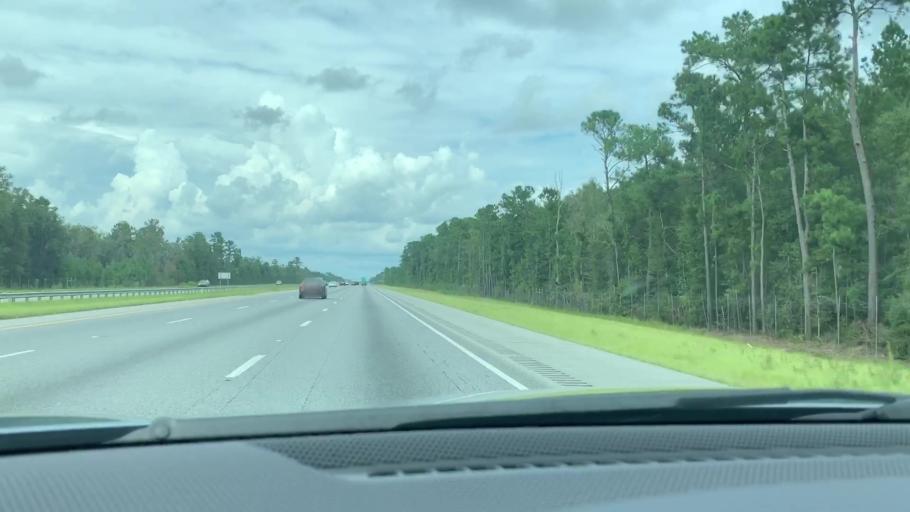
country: US
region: Georgia
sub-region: McIntosh County
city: Darien
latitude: 31.5041
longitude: -81.4458
